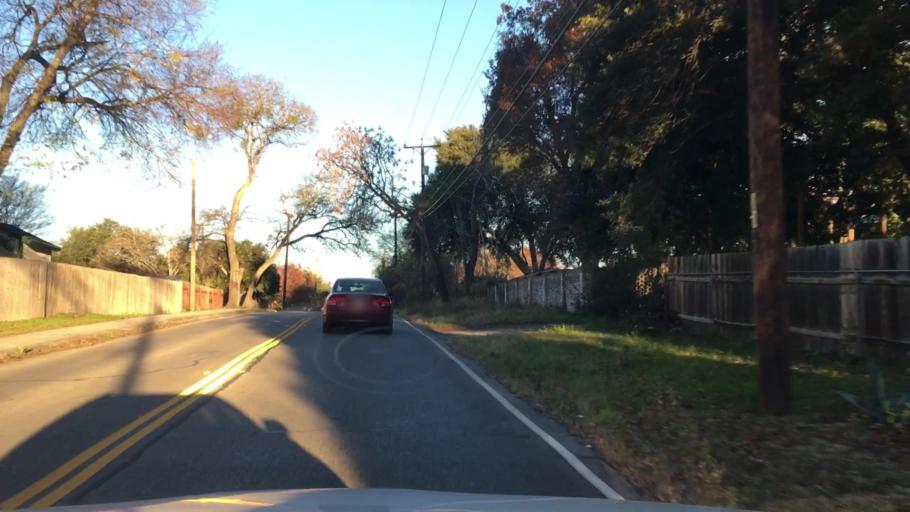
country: US
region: Texas
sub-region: Bexar County
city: Castle Hills
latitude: 29.5362
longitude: -98.5029
